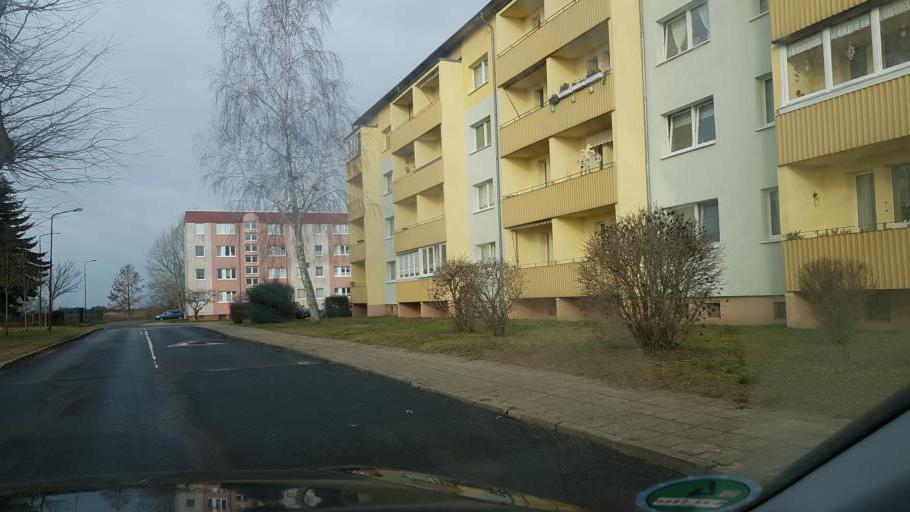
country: DE
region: Brandenburg
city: Kyritz
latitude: 52.9478
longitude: 12.3807
